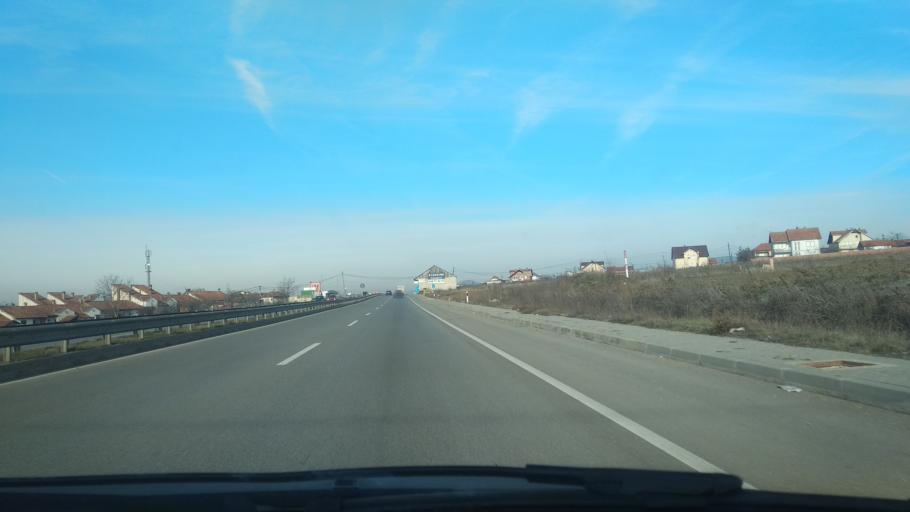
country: XK
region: Pristina
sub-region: Komuna e Obiliqit
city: Obiliq
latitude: 42.7573
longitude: 21.0342
